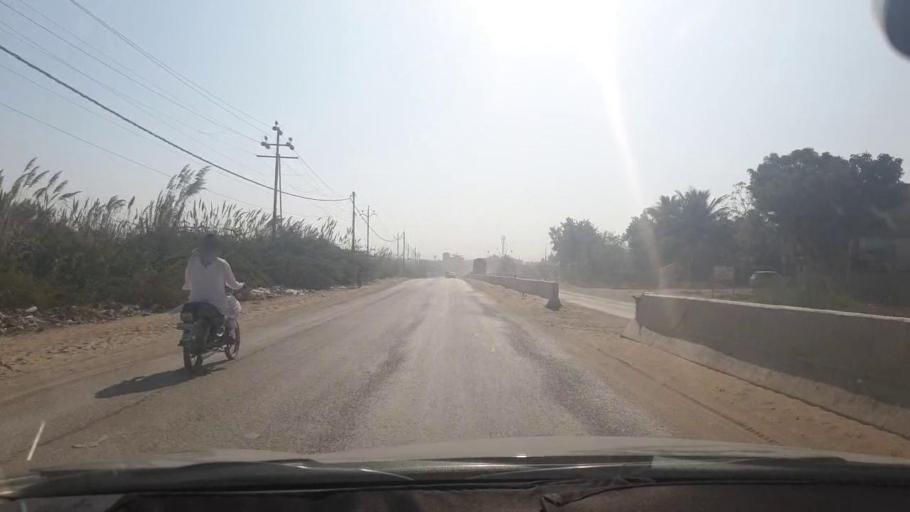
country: PK
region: Sindh
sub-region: Karachi District
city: Karachi
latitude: 25.0037
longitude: 67.0337
